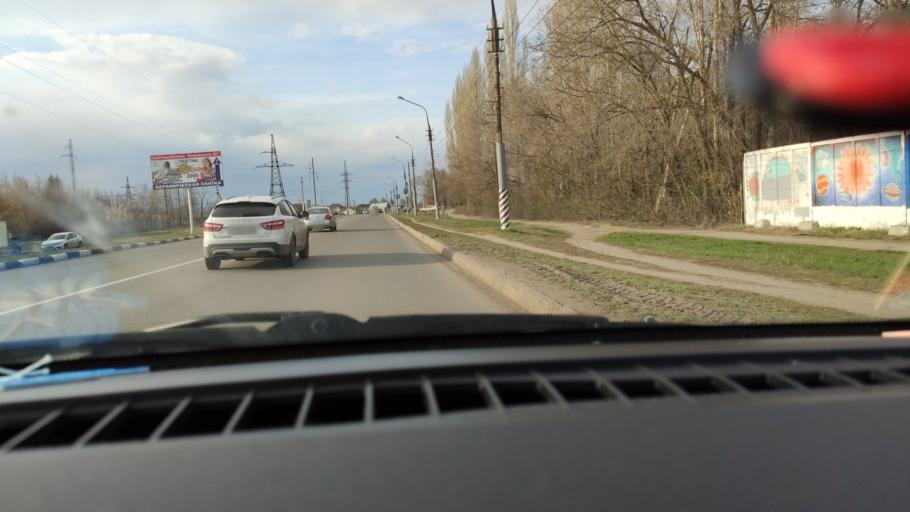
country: RU
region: Saratov
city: Privolzhskiy
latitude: 51.3966
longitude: 46.0343
